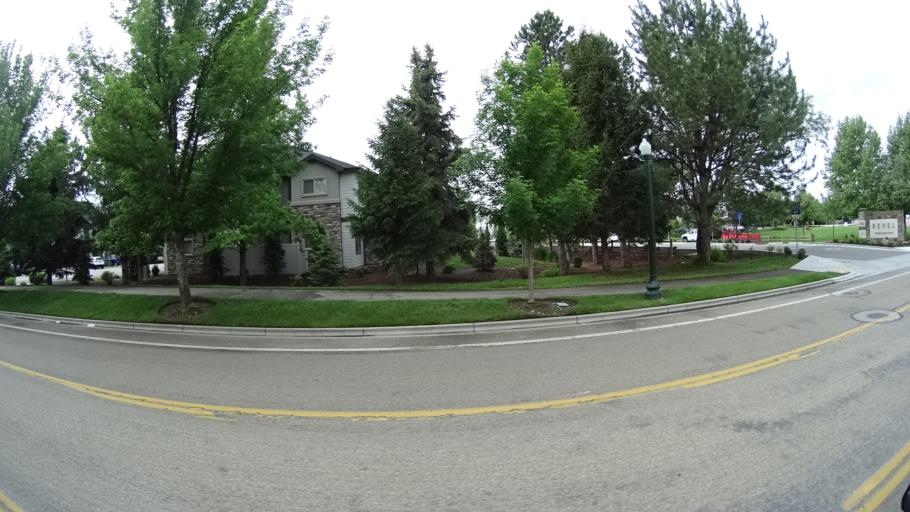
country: US
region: Idaho
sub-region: Ada County
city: Eagle
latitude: 43.6886
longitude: -116.3438
